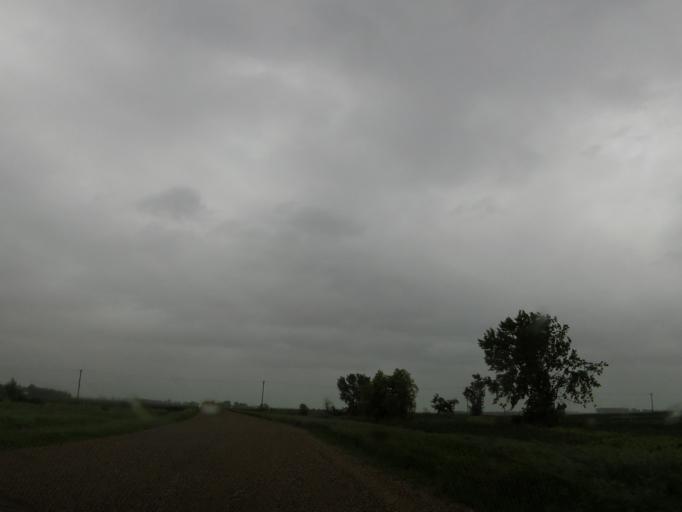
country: US
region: North Dakota
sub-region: Walsh County
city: Grafton
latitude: 48.4396
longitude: -97.4047
